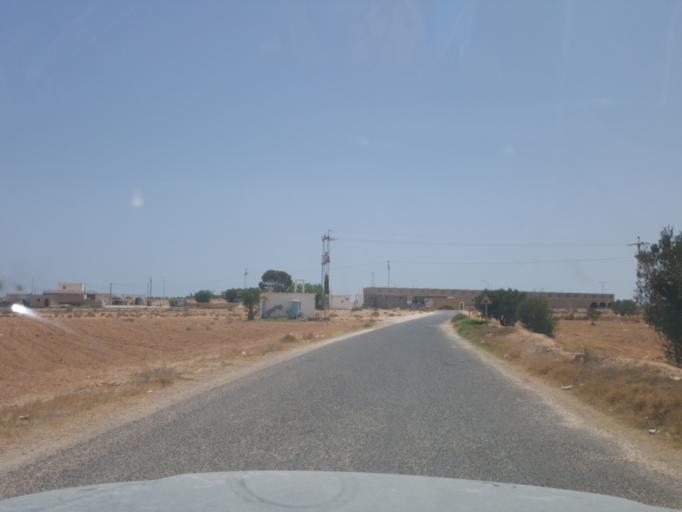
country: TN
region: Qabis
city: Gabes
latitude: 34.0547
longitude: 9.9837
